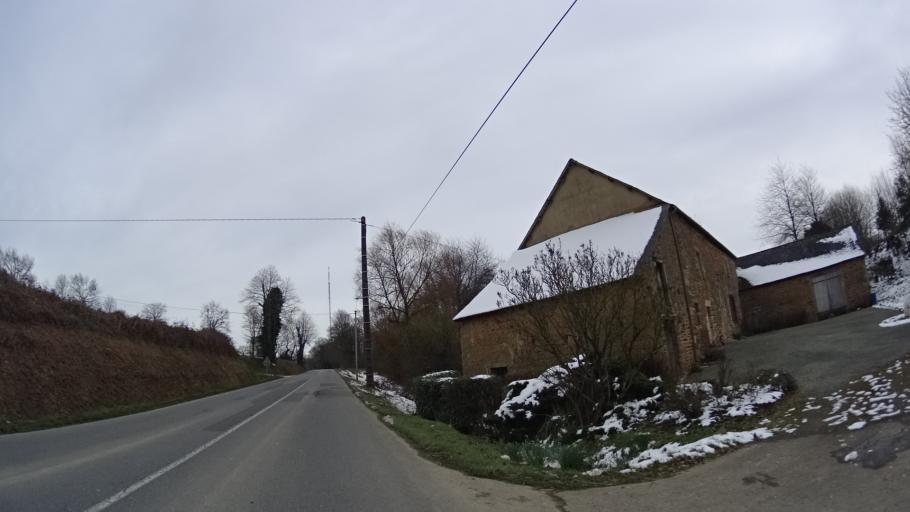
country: FR
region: Brittany
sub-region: Departement d'Ille-et-Vilaine
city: Irodouer
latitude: 48.2814
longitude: -1.9717
